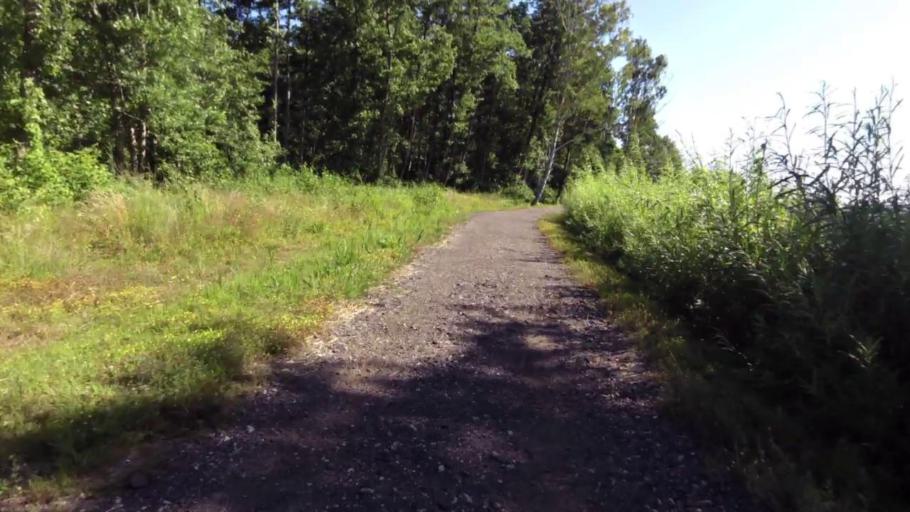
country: PL
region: West Pomeranian Voivodeship
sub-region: Powiat koszalinski
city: Mielno
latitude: 54.2790
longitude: 16.1238
